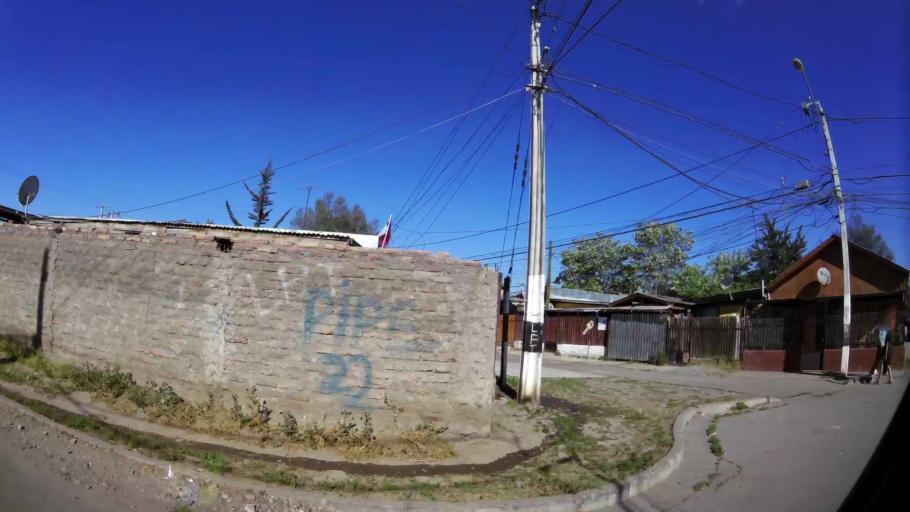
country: CL
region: Santiago Metropolitan
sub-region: Provincia de Talagante
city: Penaflor
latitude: -33.6096
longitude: -70.8721
